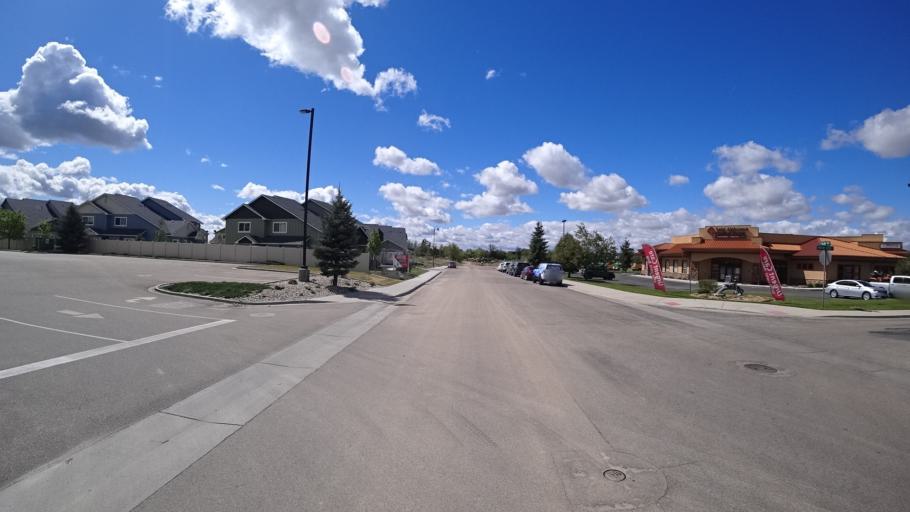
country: US
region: Idaho
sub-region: Ada County
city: Kuna
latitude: 43.4877
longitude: -116.4039
